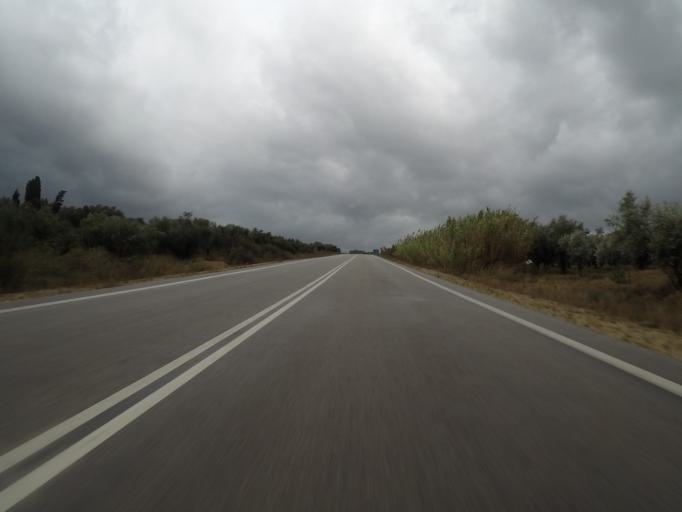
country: GR
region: Peloponnese
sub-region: Nomos Messinias
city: Gargalianoi
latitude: 37.0126
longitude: 21.6520
